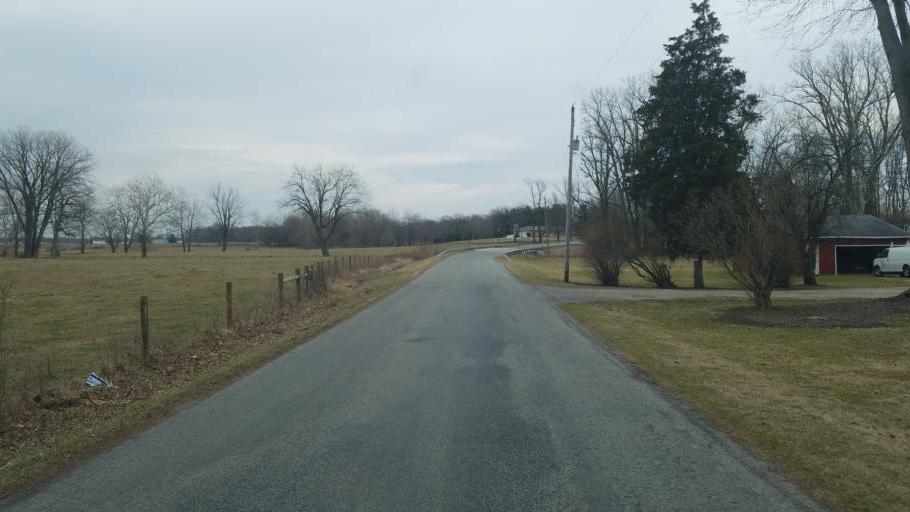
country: US
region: Ohio
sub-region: Richland County
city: Shelby
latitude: 40.8351
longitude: -82.6447
